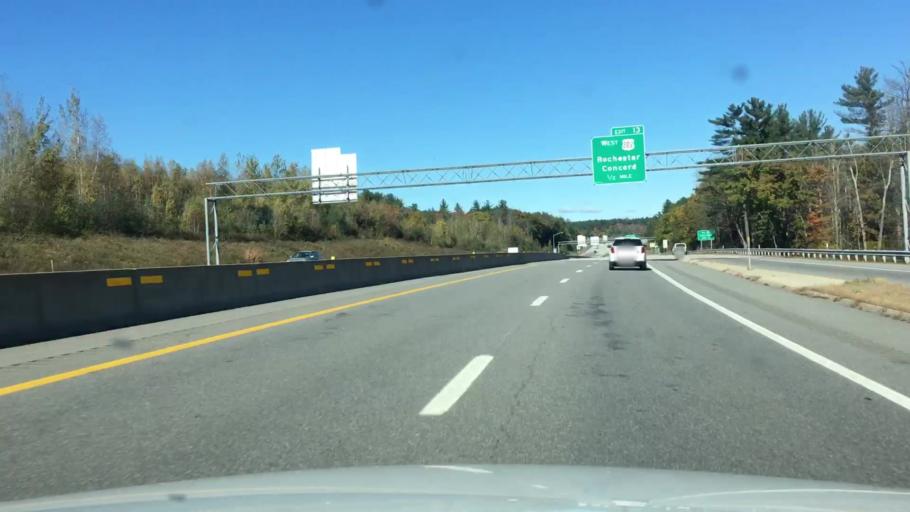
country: US
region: New Hampshire
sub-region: Strafford County
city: Rochester
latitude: 43.2850
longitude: -70.9840
